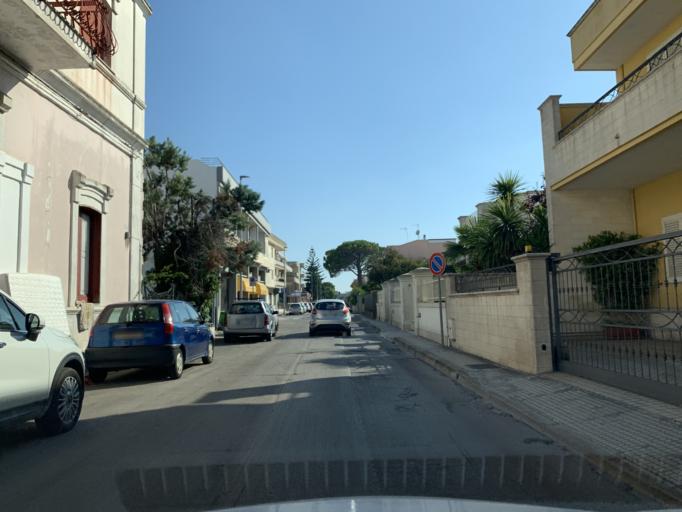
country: IT
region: Apulia
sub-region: Provincia di Lecce
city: Nardo
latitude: 40.1742
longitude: 18.0296
